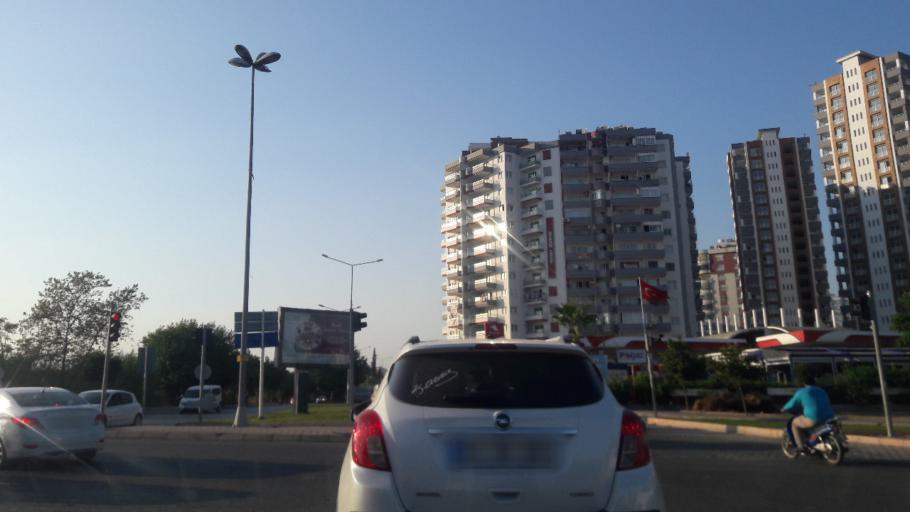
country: TR
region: Adana
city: Seyhan
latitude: 37.0107
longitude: 35.2894
